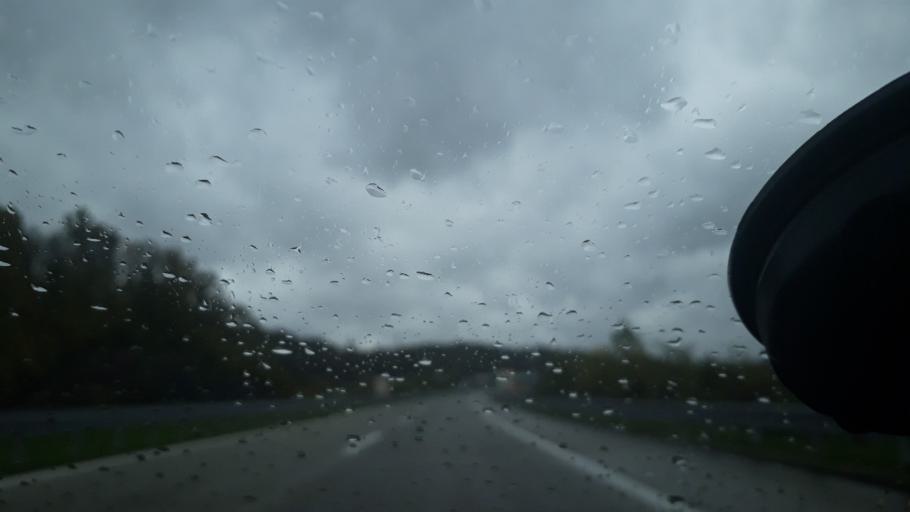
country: BA
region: Republika Srpska
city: Laktasi
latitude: 44.8875
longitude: 17.2836
